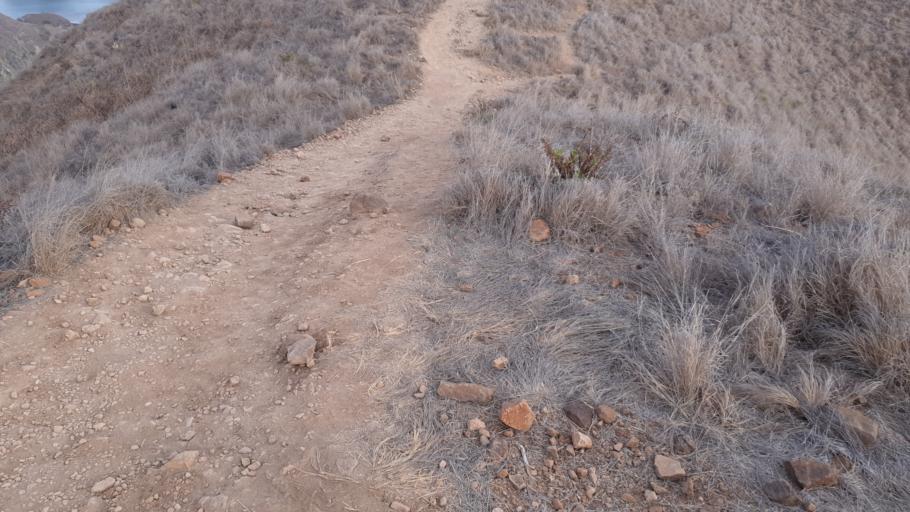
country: ID
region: East Nusa Tenggara
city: Komodo
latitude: -8.6829
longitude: 119.5574
